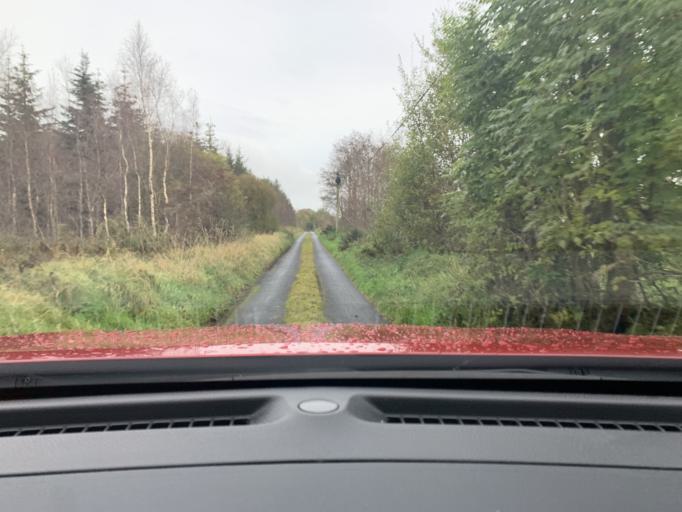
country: IE
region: Connaught
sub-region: Roscommon
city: Ballaghaderreen
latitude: 53.9200
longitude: -8.5588
